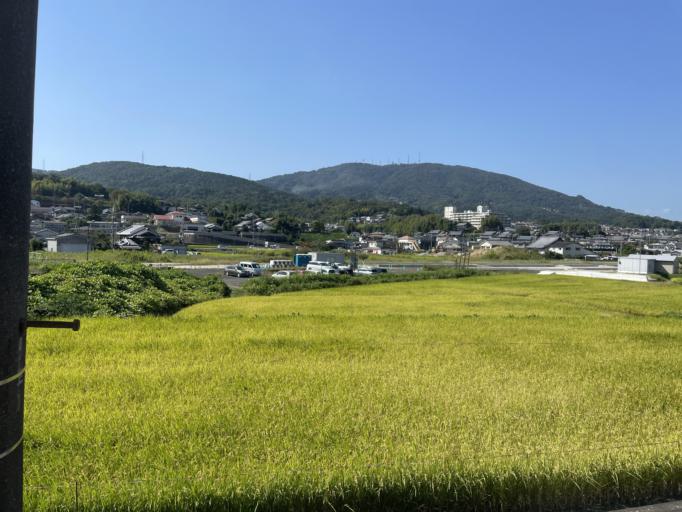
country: JP
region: Nara
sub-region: Ikoma-shi
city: Ikoma
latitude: 34.6572
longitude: 135.7090
